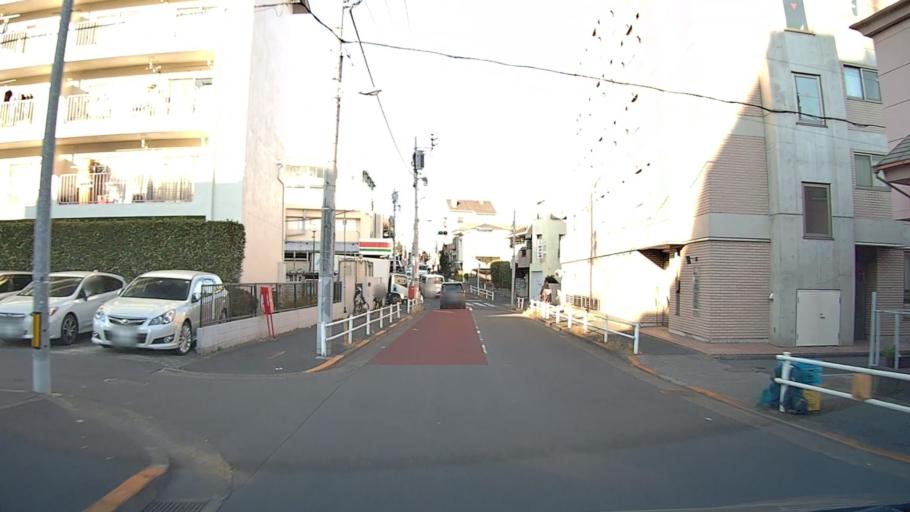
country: JP
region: Tokyo
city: Tokyo
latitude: 35.7095
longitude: 139.6731
